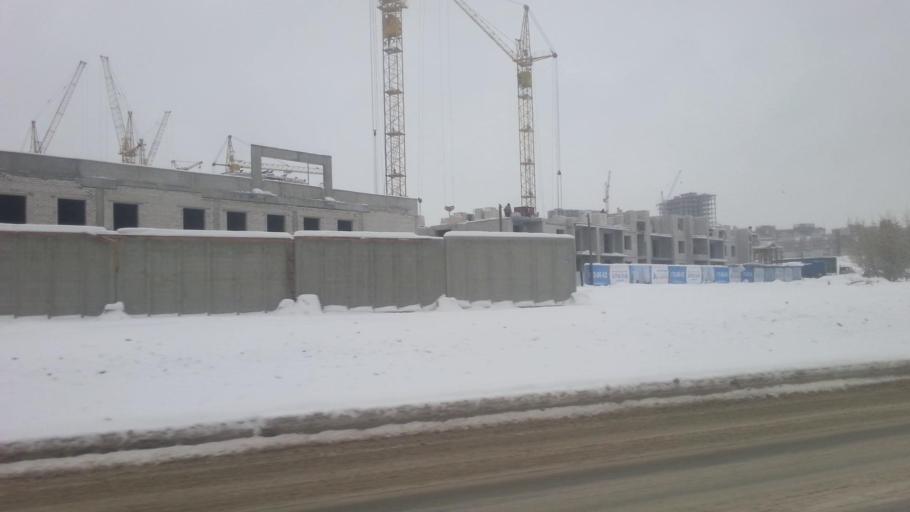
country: RU
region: Altai Krai
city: Novosilikatnyy
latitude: 53.3520
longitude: 83.6729
